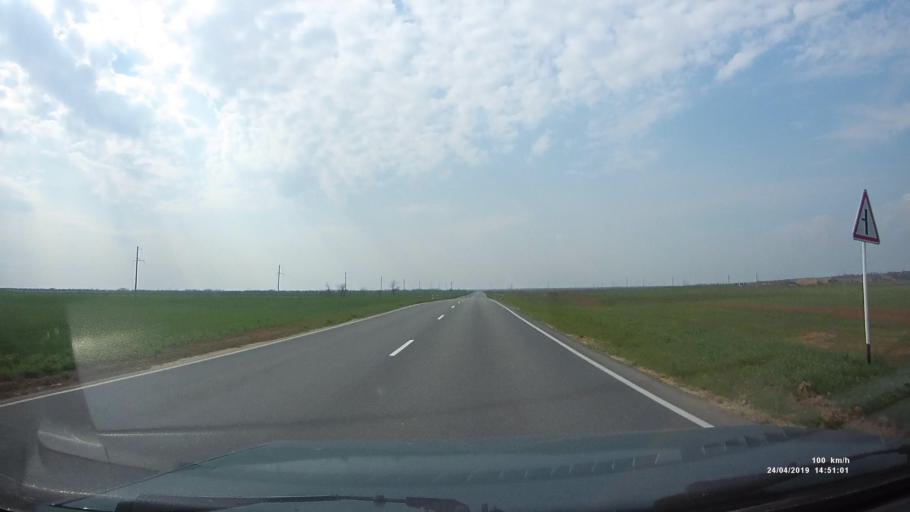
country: RU
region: Rostov
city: Remontnoye
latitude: 46.5217
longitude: 43.7086
